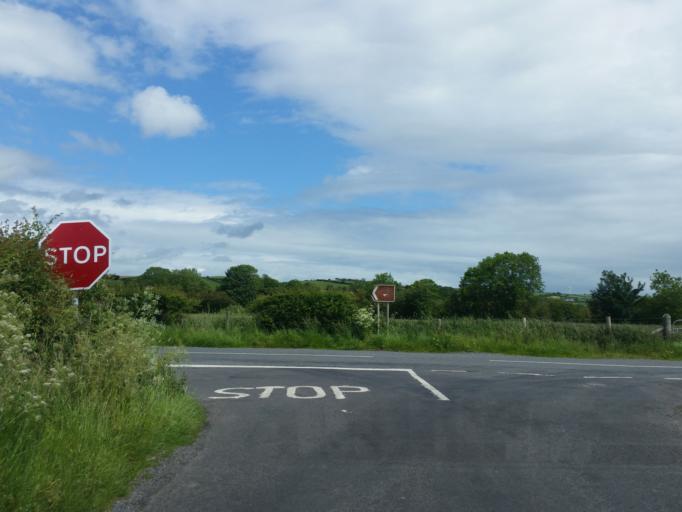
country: GB
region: Northern Ireland
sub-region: Omagh District
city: Omagh
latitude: 54.5480
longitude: -7.1174
